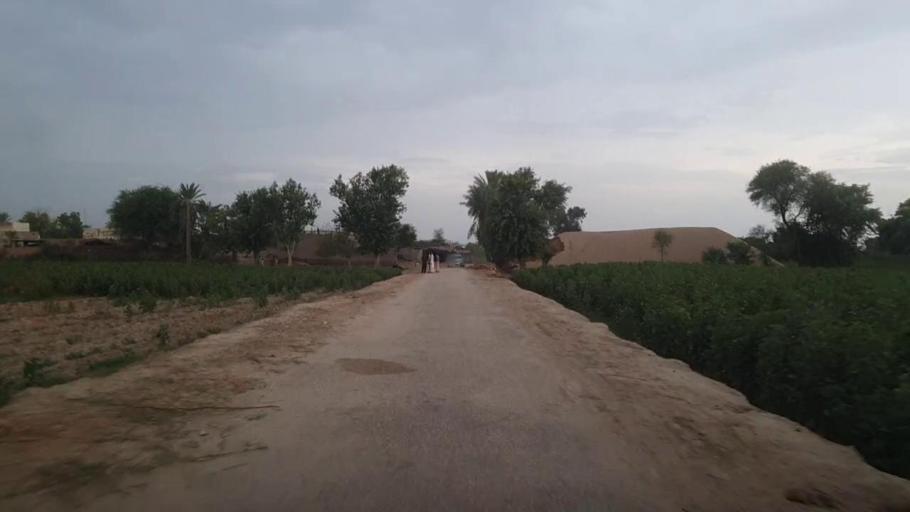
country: PK
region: Sindh
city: Karaundi
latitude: 27.0100
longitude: 68.3430
